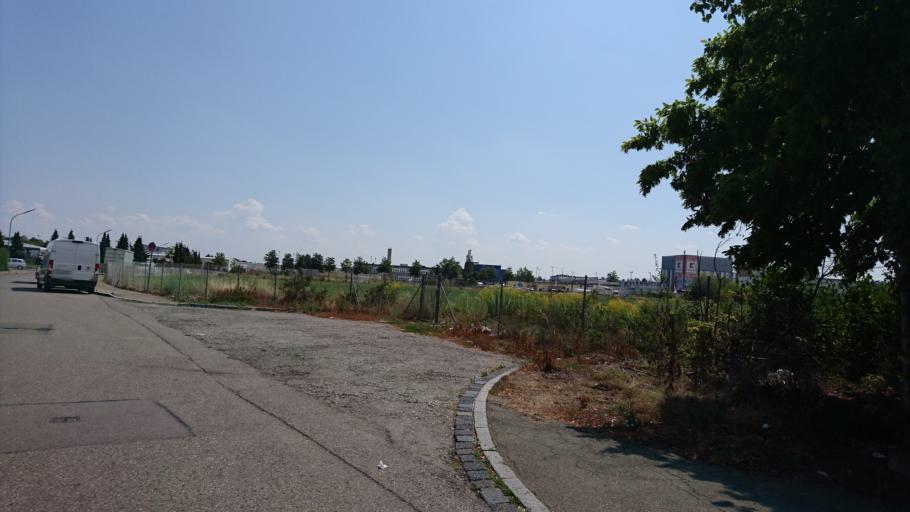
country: DE
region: Bavaria
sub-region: Swabia
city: Augsburg
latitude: 48.3836
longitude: 10.9324
